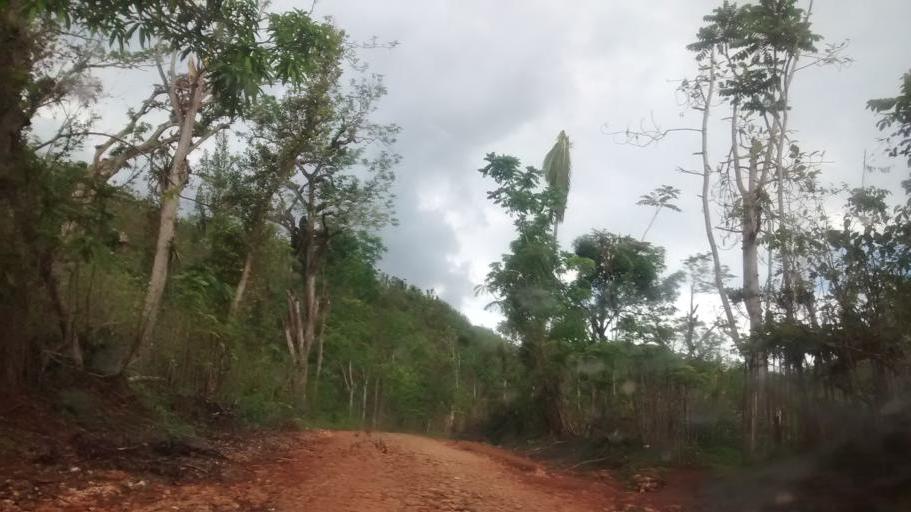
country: HT
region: Grandans
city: Corail
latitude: 18.5187
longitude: -73.7884
